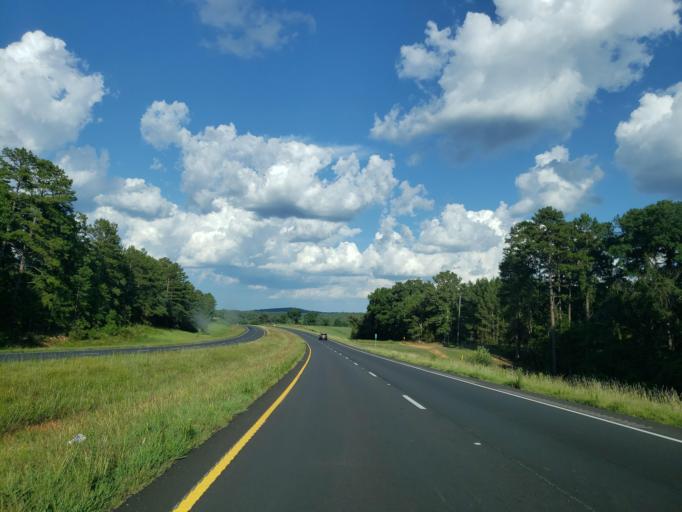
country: US
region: Georgia
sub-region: Floyd County
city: Lindale
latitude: 34.2069
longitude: -85.0870
